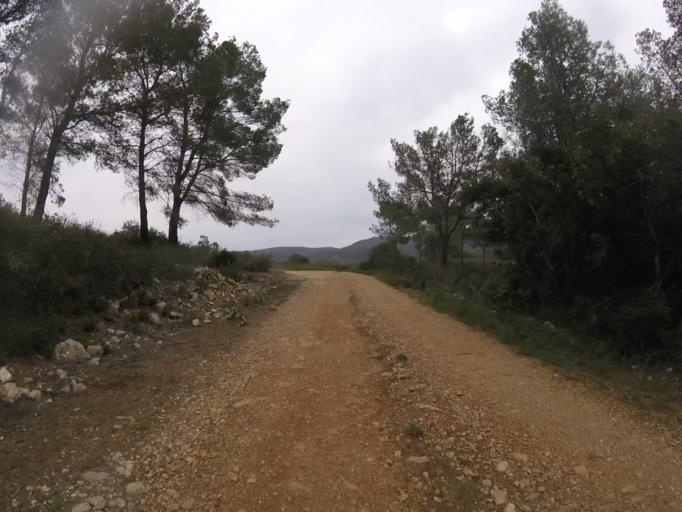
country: ES
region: Valencia
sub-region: Provincia de Castello
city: Alcala de Xivert
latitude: 40.3173
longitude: 0.2725
